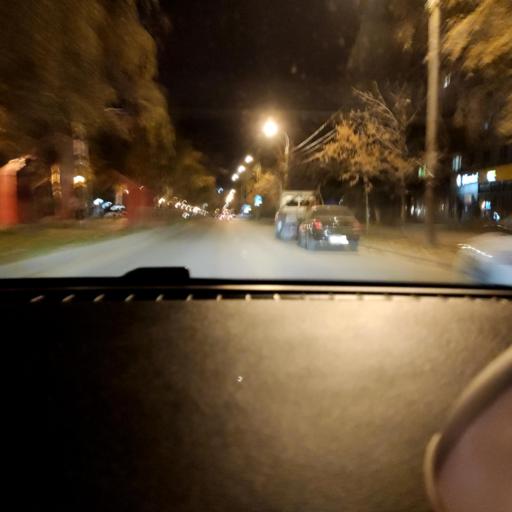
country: RU
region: Samara
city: Samara
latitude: 53.1927
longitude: 50.1791
